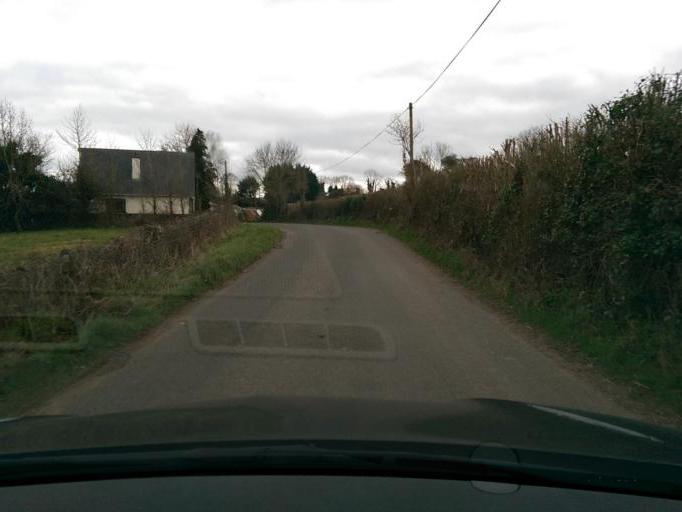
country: IE
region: Leinster
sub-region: An Iarmhi
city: Moate
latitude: 53.3873
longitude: -7.8242
